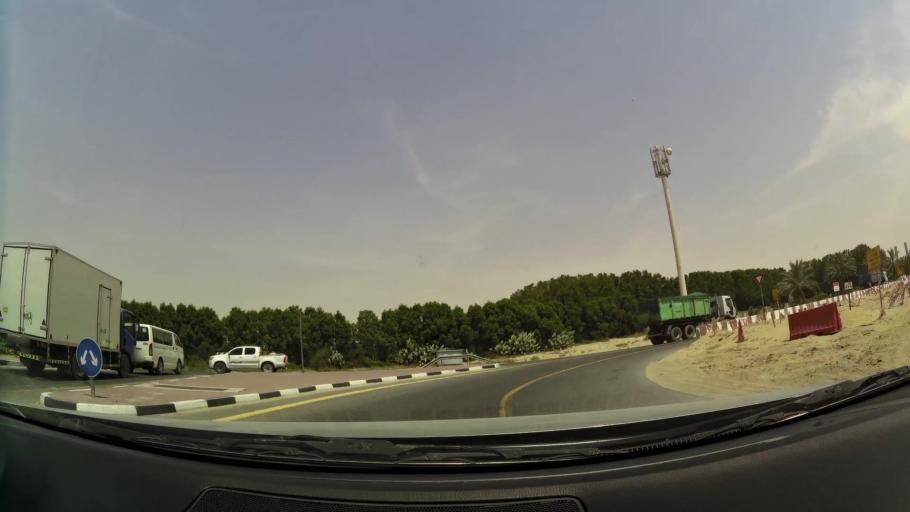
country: AE
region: Ash Shariqah
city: Sharjah
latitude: 25.1586
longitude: 55.4242
